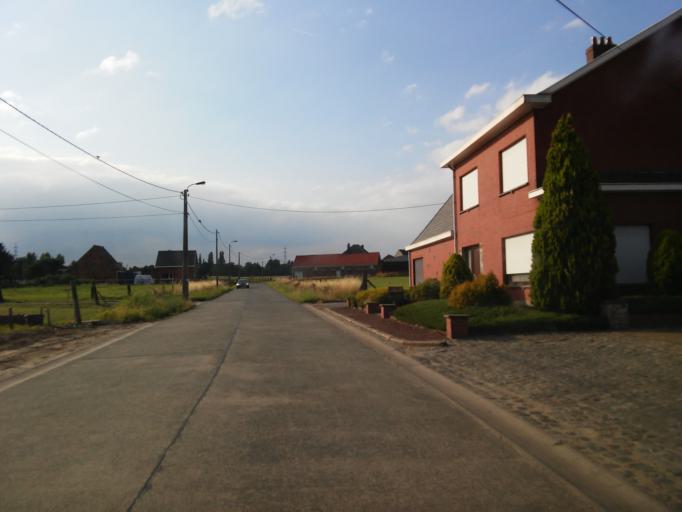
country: BE
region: Flanders
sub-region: Provincie Antwerpen
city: Rumst
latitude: 51.0920
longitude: 4.4599
